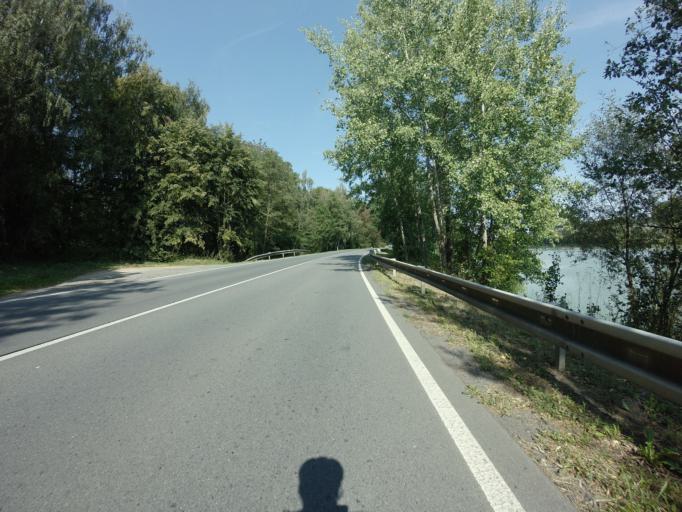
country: CZ
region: Central Bohemia
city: Sedlcany
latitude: 49.6441
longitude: 14.4334
